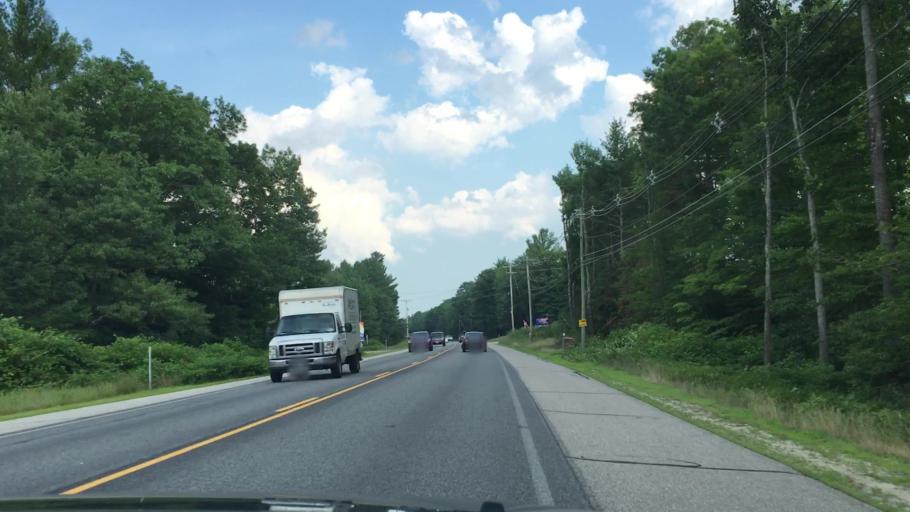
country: US
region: New Hampshire
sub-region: Strafford County
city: Farmington
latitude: 43.3769
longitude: -71.0631
